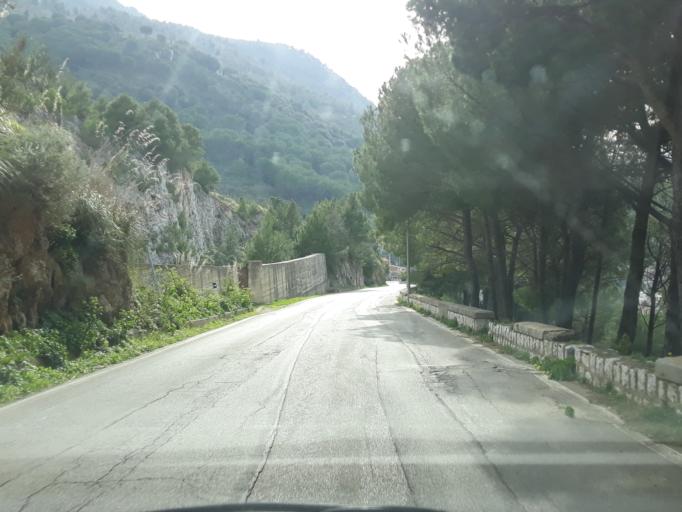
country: IT
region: Sicily
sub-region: Palermo
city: Altofonte
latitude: 38.0431
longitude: 13.3037
